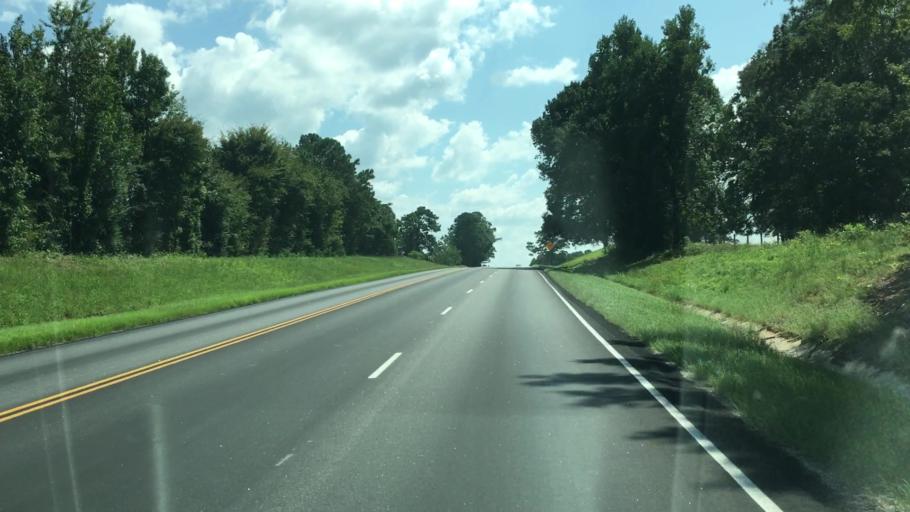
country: US
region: Georgia
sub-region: Morgan County
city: Madison
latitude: 33.6596
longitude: -83.4458
